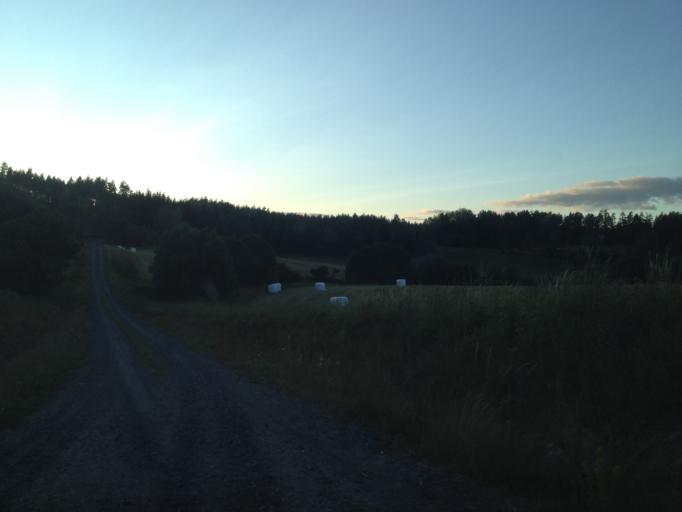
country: SE
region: Kalmar
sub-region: Vasterviks Kommun
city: Overum
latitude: 58.0198
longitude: 16.1205
